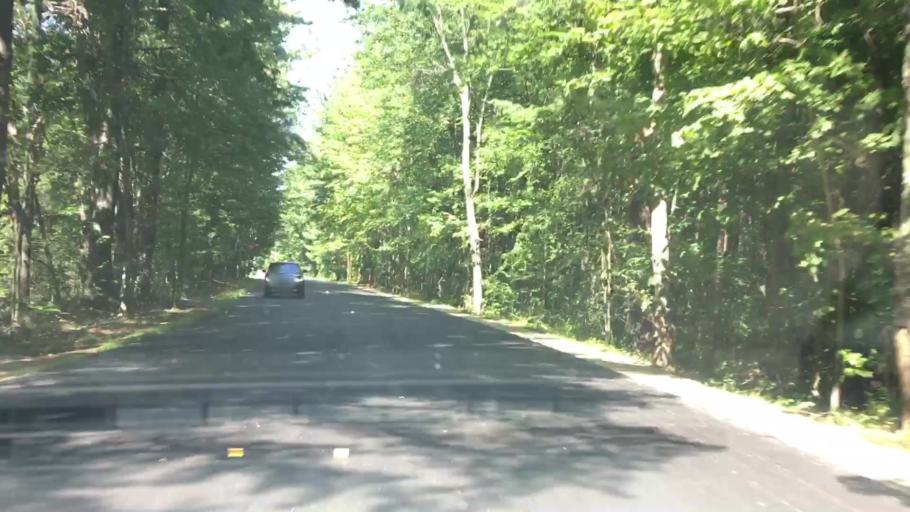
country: US
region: Maine
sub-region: York County
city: Eliot
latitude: 43.1576
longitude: -70.8393
